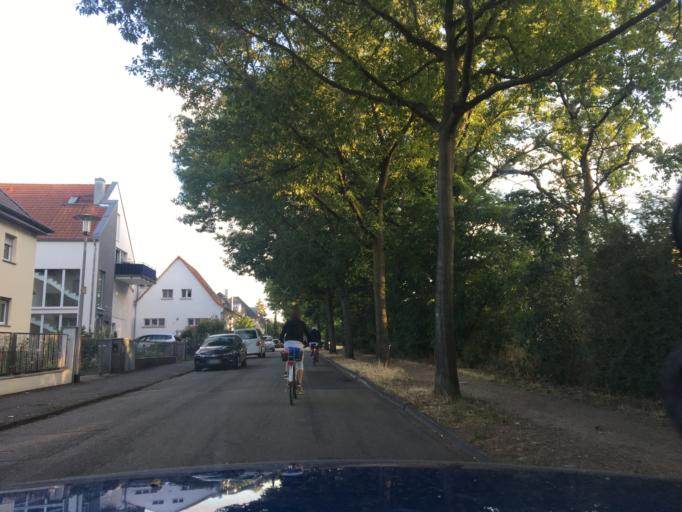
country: DE
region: Hesse
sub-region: Regierungsbezirk Darmstadt
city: Darmstadt
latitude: 49.8864
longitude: 8.6745
